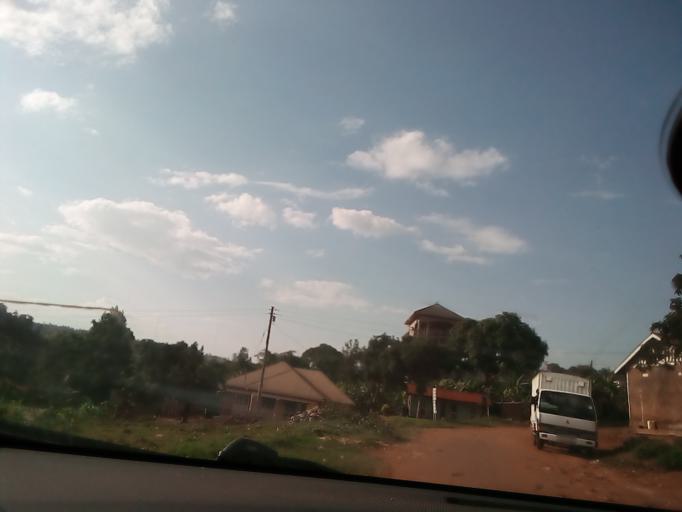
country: UG
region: Central Region
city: Masaka
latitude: -0.3546
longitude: 31.7443
